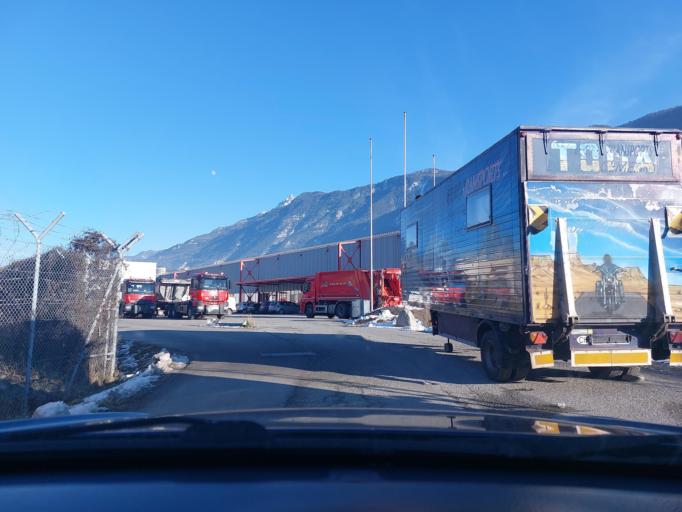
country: CH
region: Valais
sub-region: Martigny District
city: Martigny-Ville
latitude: 46.1102
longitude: 7.0898
